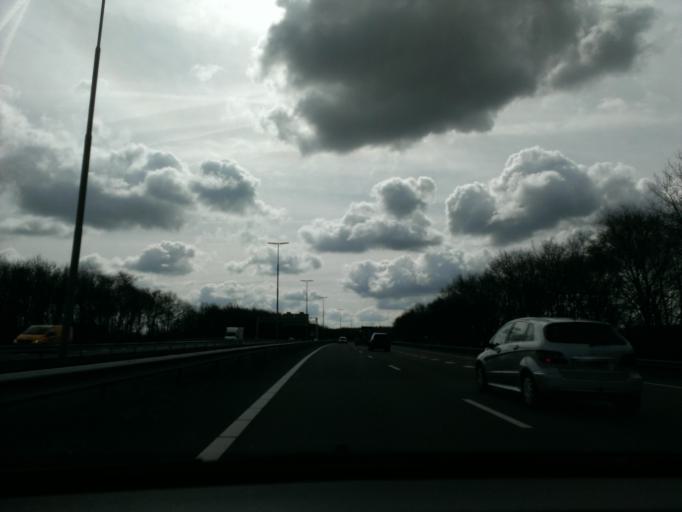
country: NL
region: Gelderland
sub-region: Gemeente Hattem
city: Hattem
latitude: 52.4799
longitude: 6.0322
